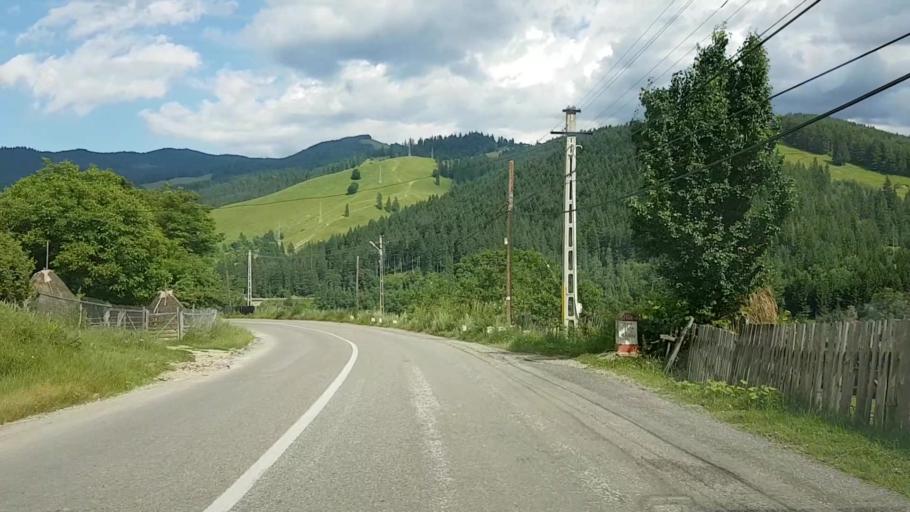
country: RO
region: Neamt
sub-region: Comuna Hangu
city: Hangu
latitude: 47.0178
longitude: 26.0771
